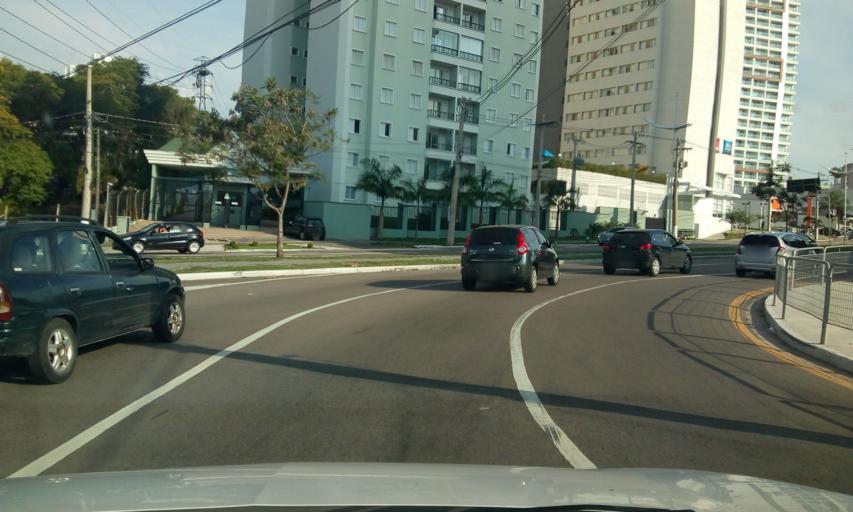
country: BR
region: Sao Paulo
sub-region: Jundiai
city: Jundiai
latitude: -23.2004
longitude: -46.8919
